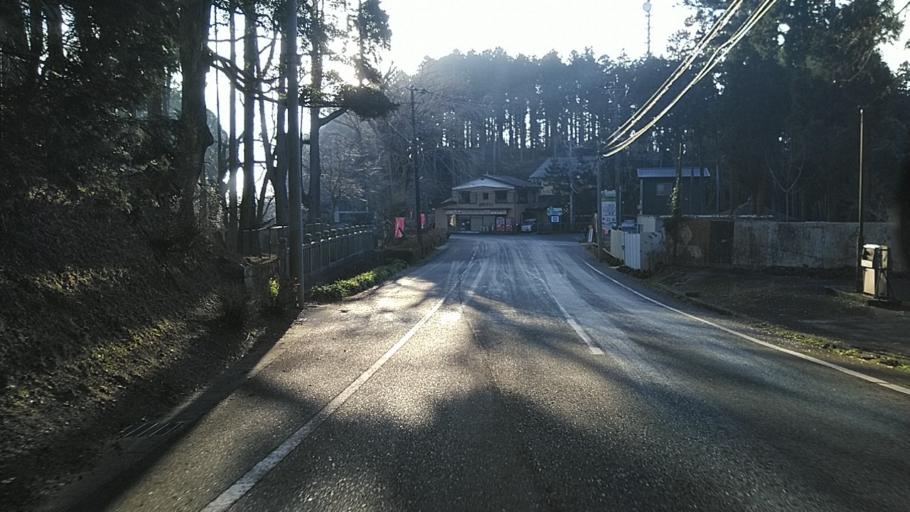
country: JP
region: Chiba
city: Kimitsu
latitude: 35.2544
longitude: 139.9627
